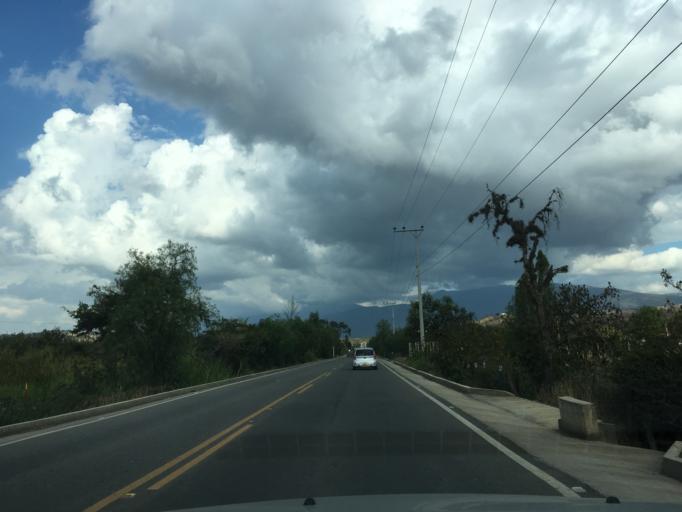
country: CO
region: Boyaca
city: Sutamarchan
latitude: 5.6222
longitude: -73.5998
